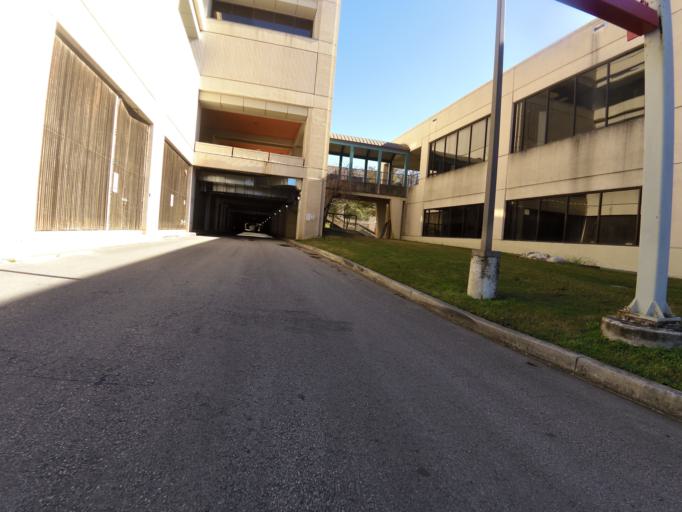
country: US
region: Texas
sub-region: Bexar County
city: Shavano Park
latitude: 29.5845
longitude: -98.6198
